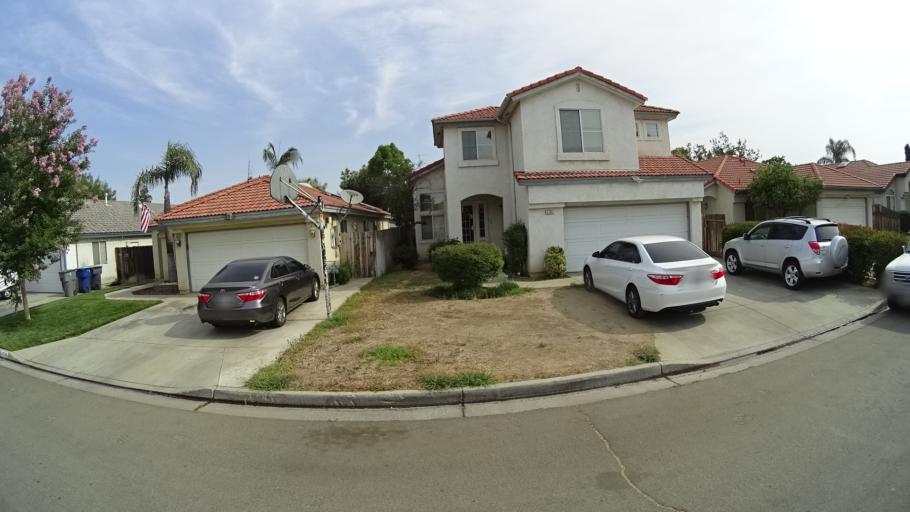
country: US
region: California
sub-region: Fresno County
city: West Park
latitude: 36.7686
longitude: -119.8687
